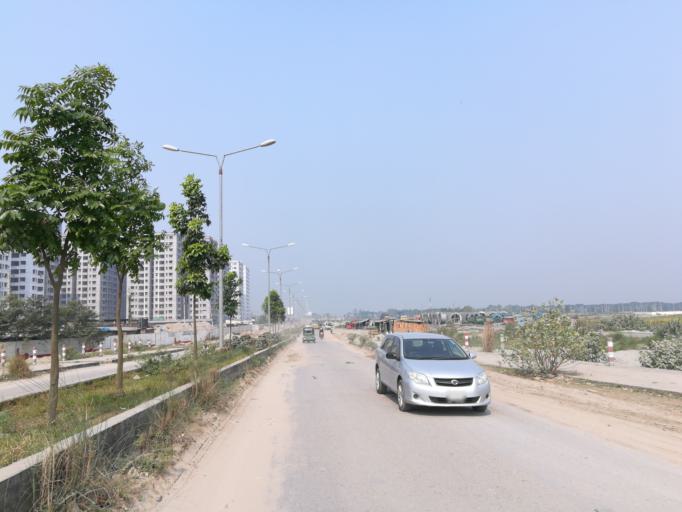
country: BD
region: Dhaka
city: Tungi
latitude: 23.8589
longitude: 90.3575
